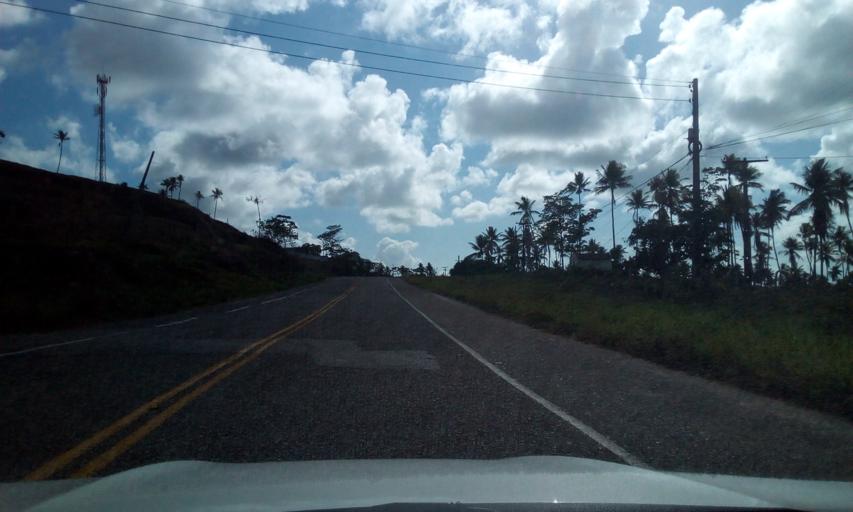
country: BR
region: Sergipe
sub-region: Indiaroba
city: Indiaroba
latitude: -11.5164
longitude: -37.5192
